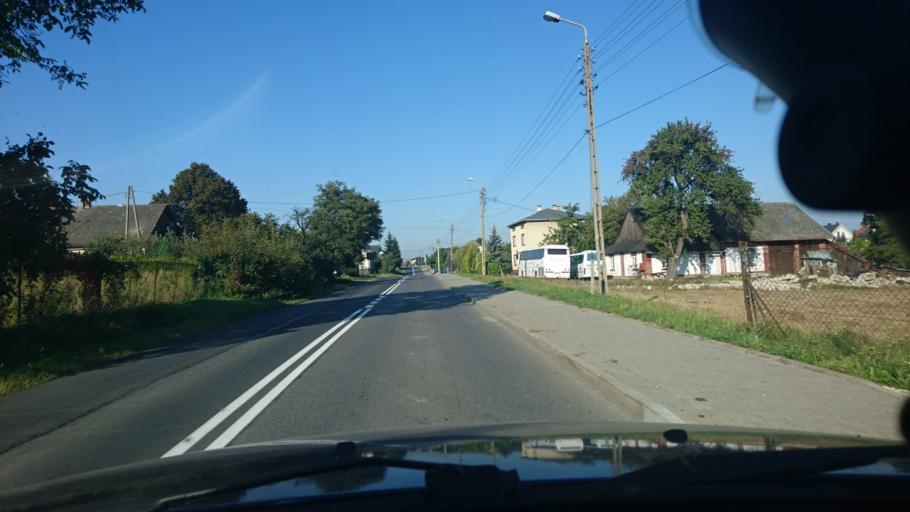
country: PL
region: Silesian Voivodeship
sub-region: Bielsko-Biala
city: Bielsko-Biala
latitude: 49.8507
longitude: 19.0626
